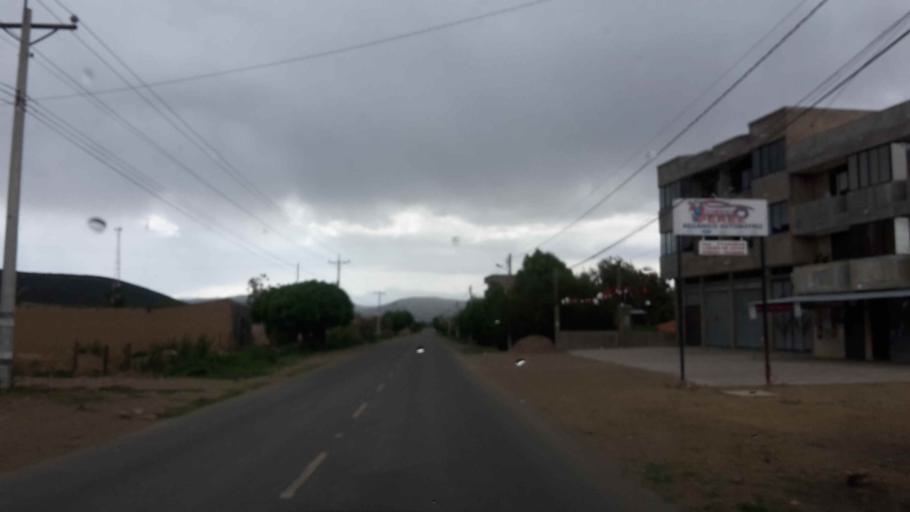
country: BO
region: Cochabamba
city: Tarata
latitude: -17.5883
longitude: -66.0483
